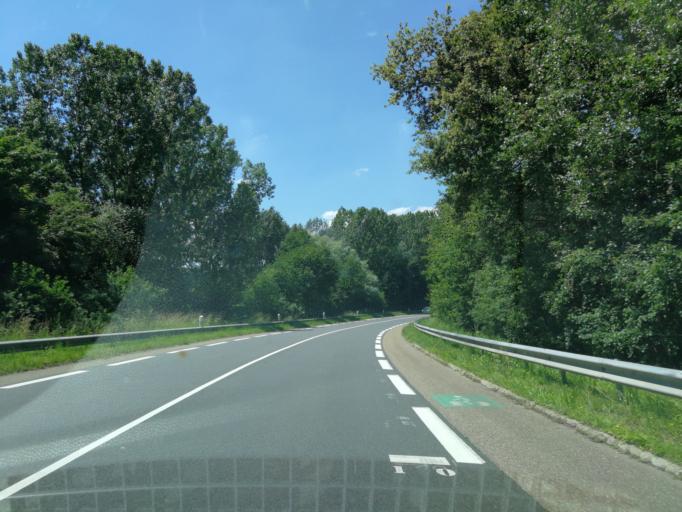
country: FR
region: Ile-de-France
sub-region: Departement de l'Essonne
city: Briis-sous-Forges
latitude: 48.6161
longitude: 2.1210
